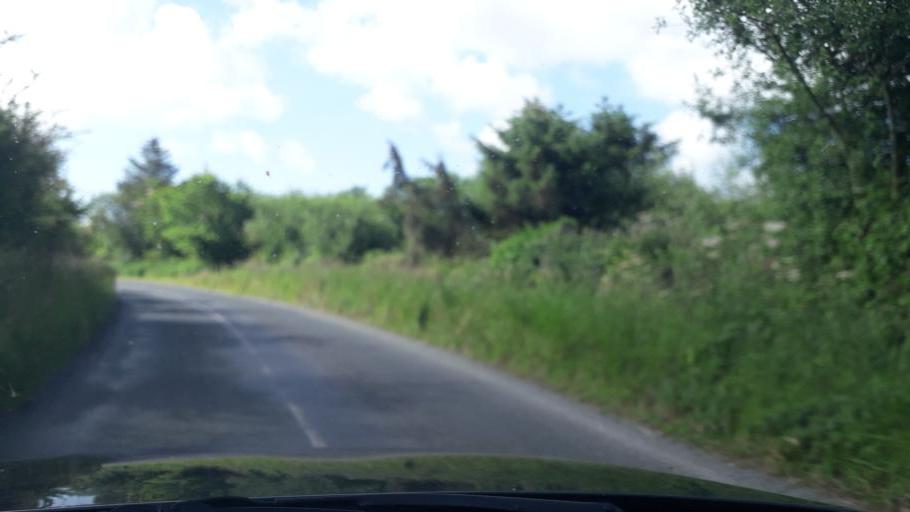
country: IE
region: Leinster
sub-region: Loch Garman
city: Loch Garman
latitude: 52.2589
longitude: -6.5548
